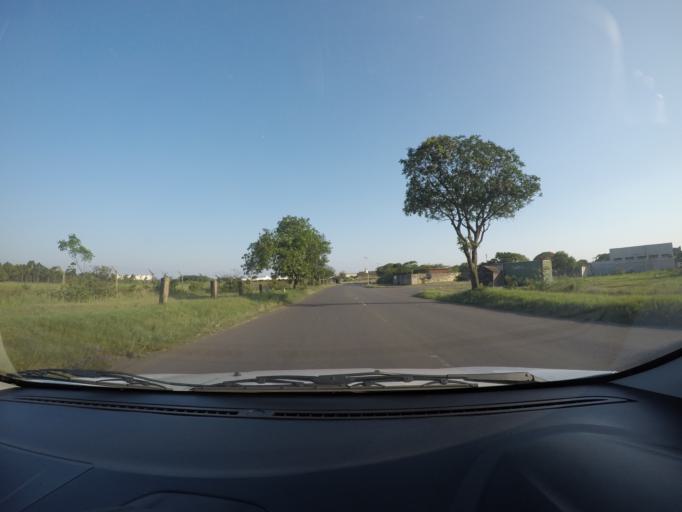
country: ZA
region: KwaZulu-Natal
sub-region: uThungulu District Municipality
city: Richards Bay
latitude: -28.7656
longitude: 32.0089
